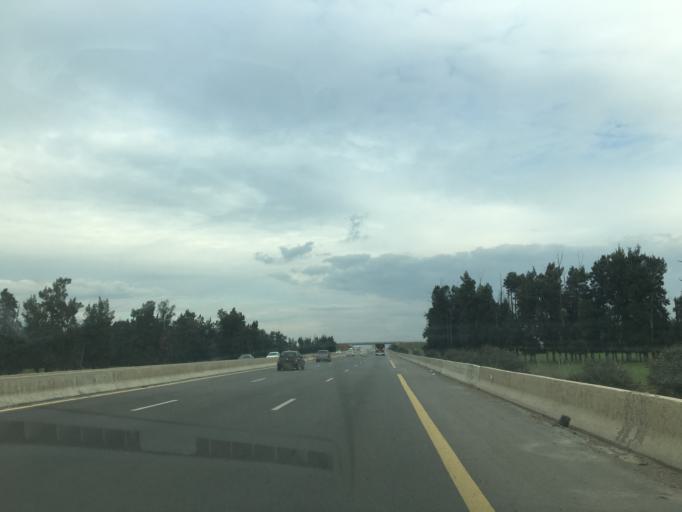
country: DZ
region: Bouira
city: Bouira
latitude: 36.3280
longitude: 3.9646
